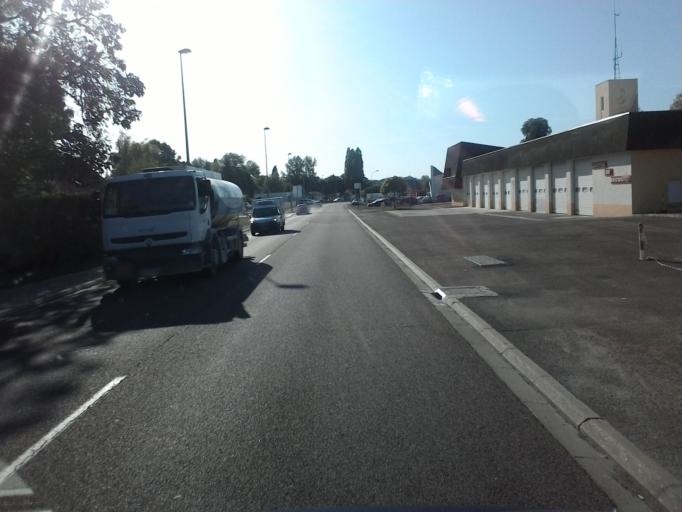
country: FR
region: Champagne-Ardenne
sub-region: Departement de l'Aube
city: Bar-sur-Seine
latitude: 48.1194
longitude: 4.3725
